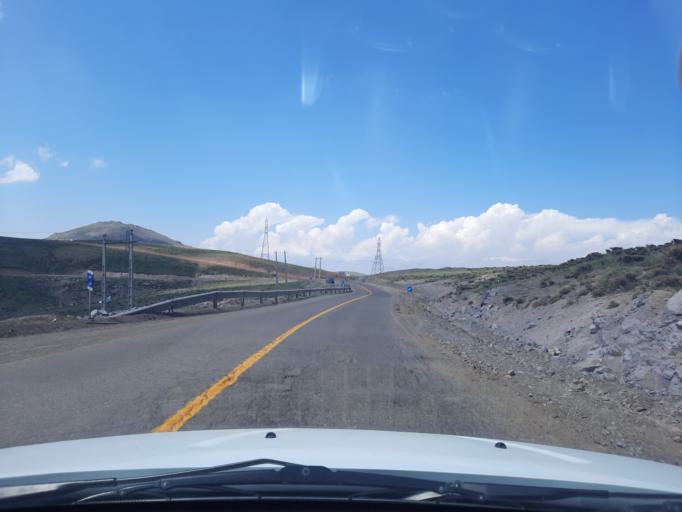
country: IR
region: Qazvin
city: Qazvin
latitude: 36.3913
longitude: 50.2079
